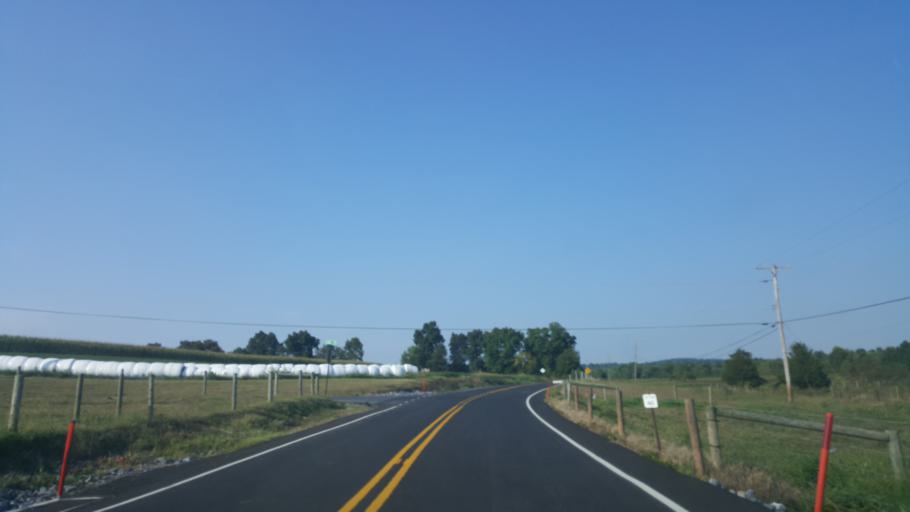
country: US
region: Pennsylvania
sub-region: Lebanon County
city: Campbelltown
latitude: 40.2189
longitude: -76.5584
